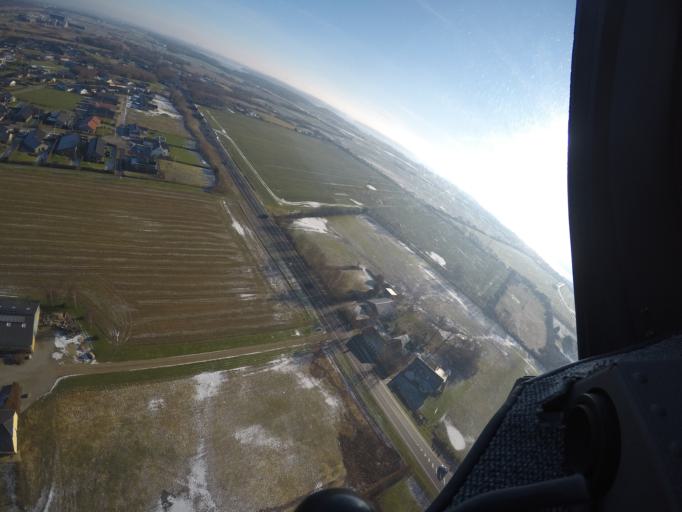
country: DK
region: South Denmark
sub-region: Fredericia Kommune
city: Taulov
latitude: 55.5329
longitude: 9.6235
